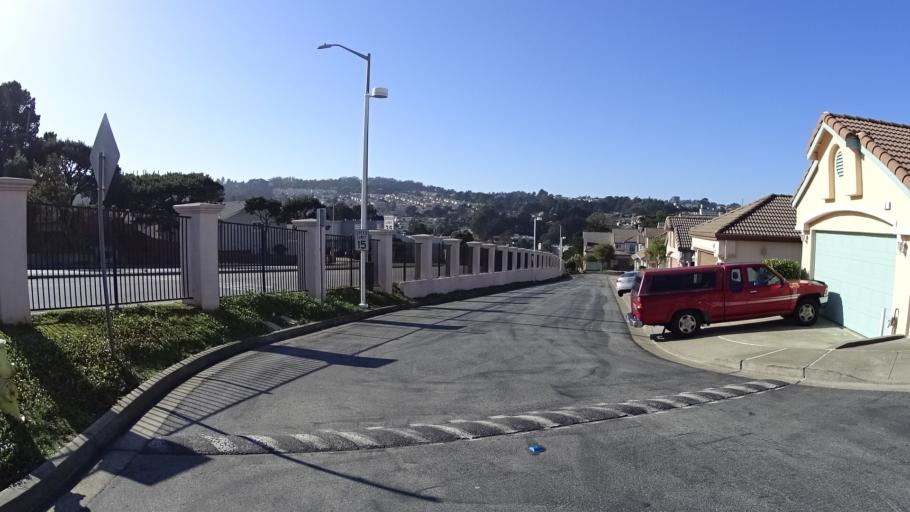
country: US
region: California
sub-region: San Mateo County
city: Colma
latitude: 37.6421
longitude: -122.4497
